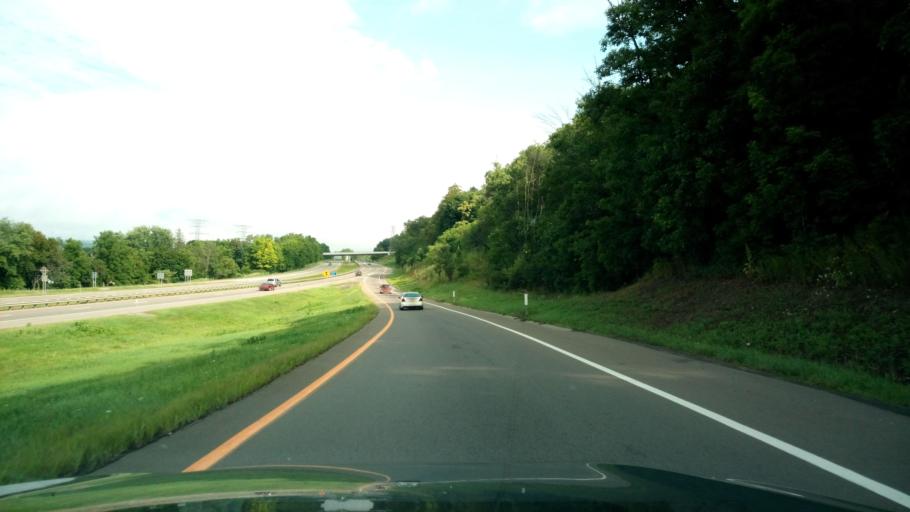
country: US
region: New York
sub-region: Chemung County
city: Elmira
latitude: 42.0968
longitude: -76.7865
